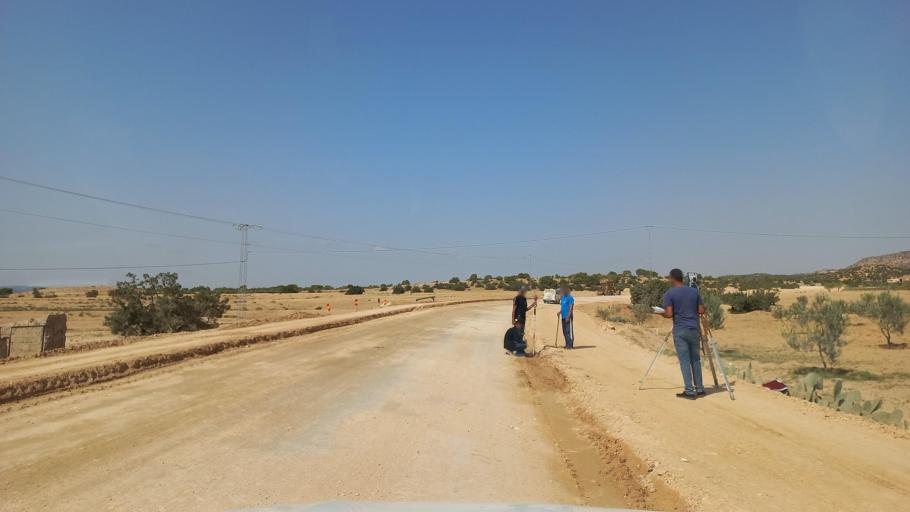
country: TN
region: Al Qasrayn
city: Sbiba
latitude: 35.4027
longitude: 8.9986
